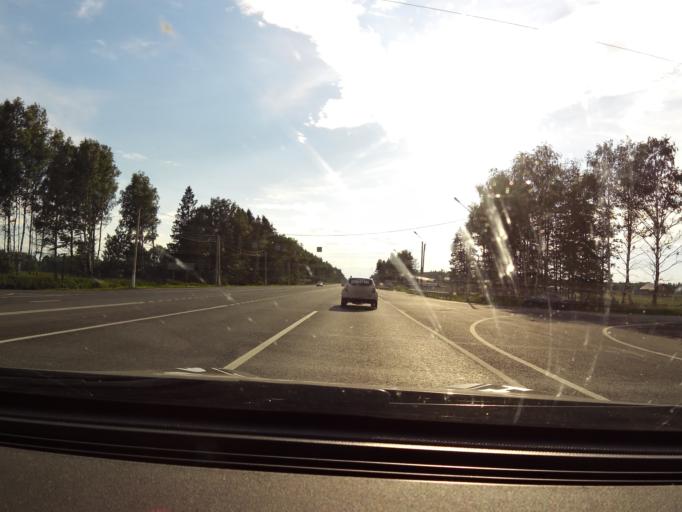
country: RU
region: Vladimir
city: Krasnyy Oktyabr'
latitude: 56.2191
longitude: 41.4753
